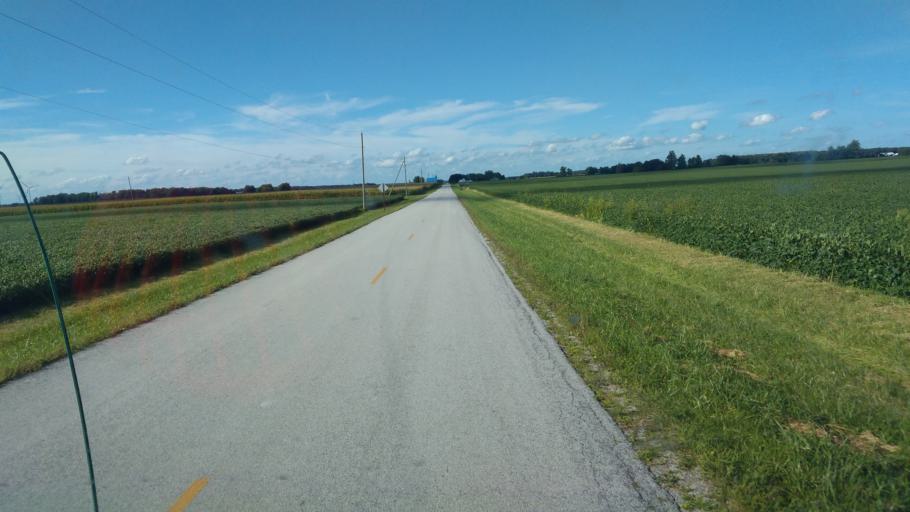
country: US
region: Ohio
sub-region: Hardin County
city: Kenton
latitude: 40.7339
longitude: -83.6908
